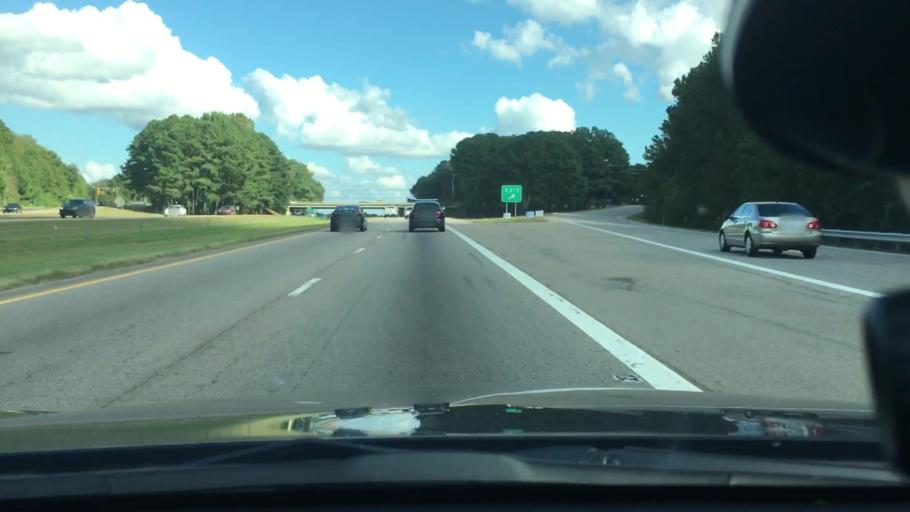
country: US
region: North Carolina
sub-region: Wake County
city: West Raleigh
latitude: 35.8041
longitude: -78.7108
